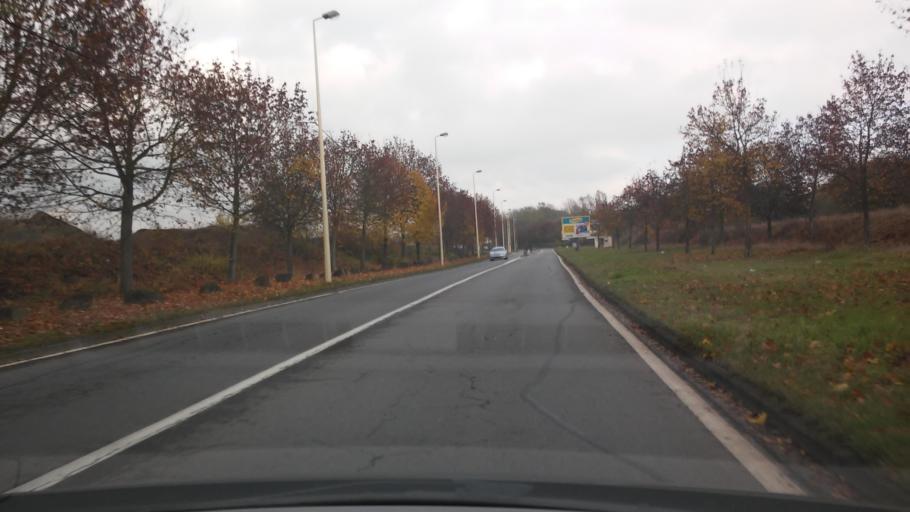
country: FR
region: Lorraine
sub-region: Departement de la Moselle
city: Terville
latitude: 49.3345
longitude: 6.1556
